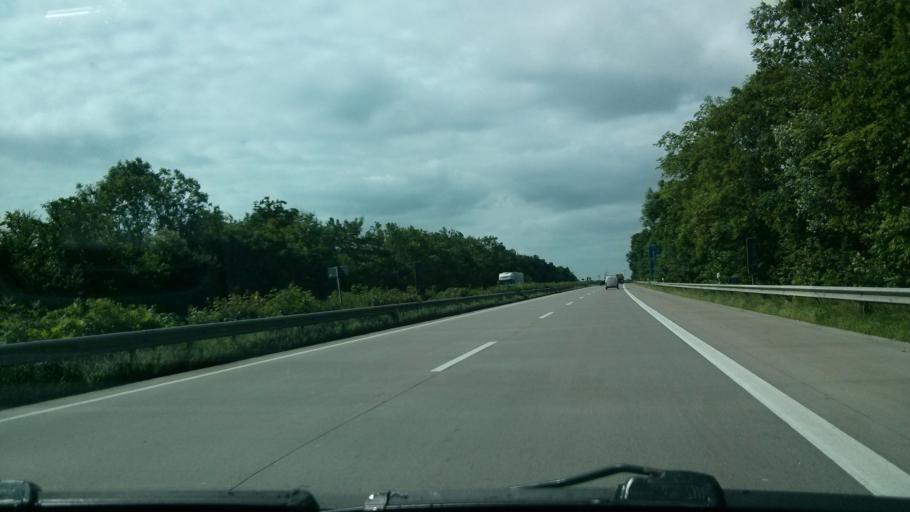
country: DE
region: Lower Saxony
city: Loxstedt
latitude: 53.4708
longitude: 8.6090
